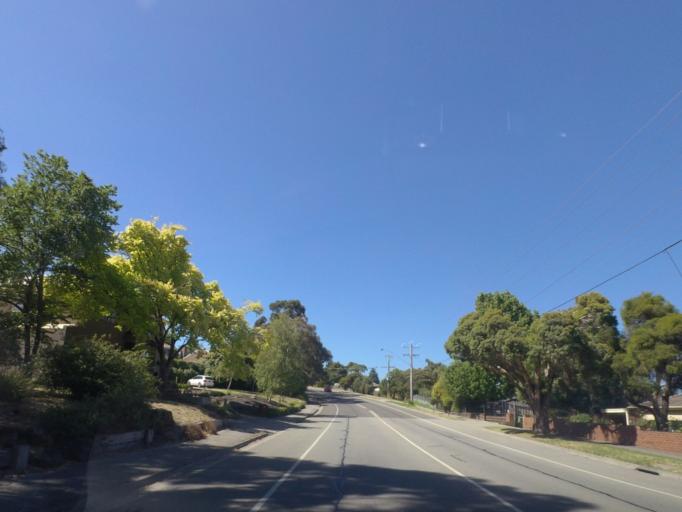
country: AU
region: Victoria
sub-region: Maroondah
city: Warranwood
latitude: -37.7909
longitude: 145.2465
